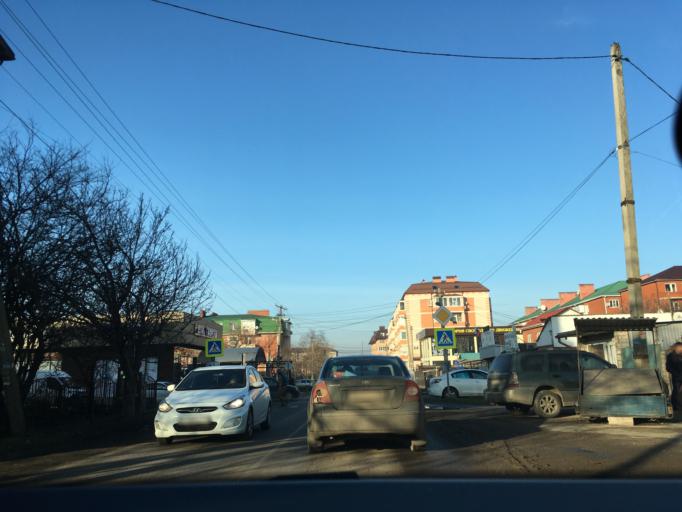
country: RU
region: Krasnodarskiy
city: Krasnodar
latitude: 45.0724
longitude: 39.0213
